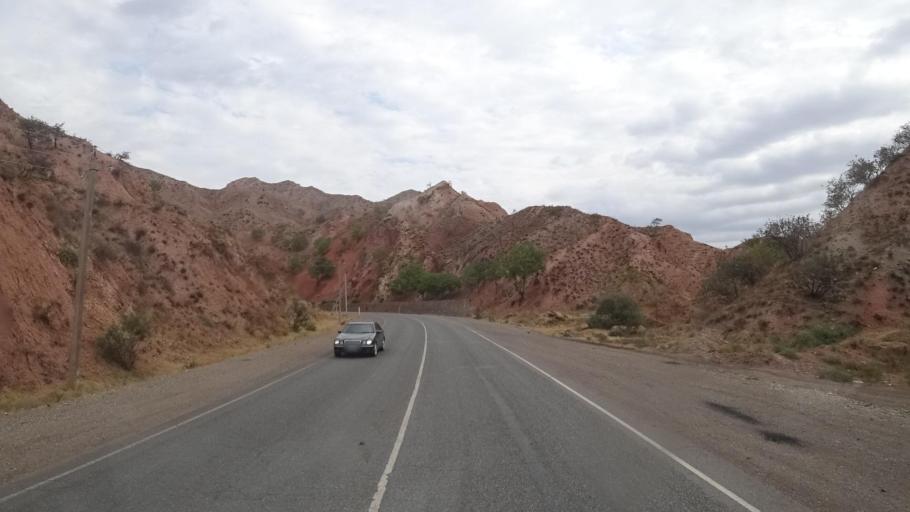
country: KG
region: Jalal-Abad
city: Tash-Kumyr
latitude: 41.3344
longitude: 72.2253
